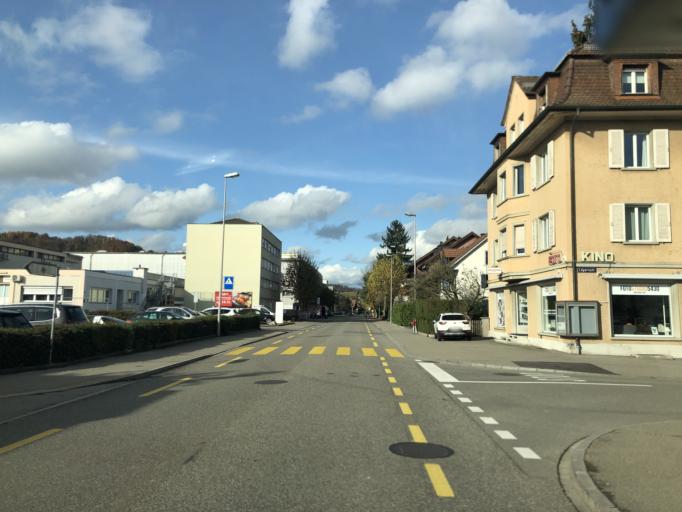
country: CH
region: Aargau
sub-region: Bezirk Baden
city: Wettingen
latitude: 47.4608
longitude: 8.3156
